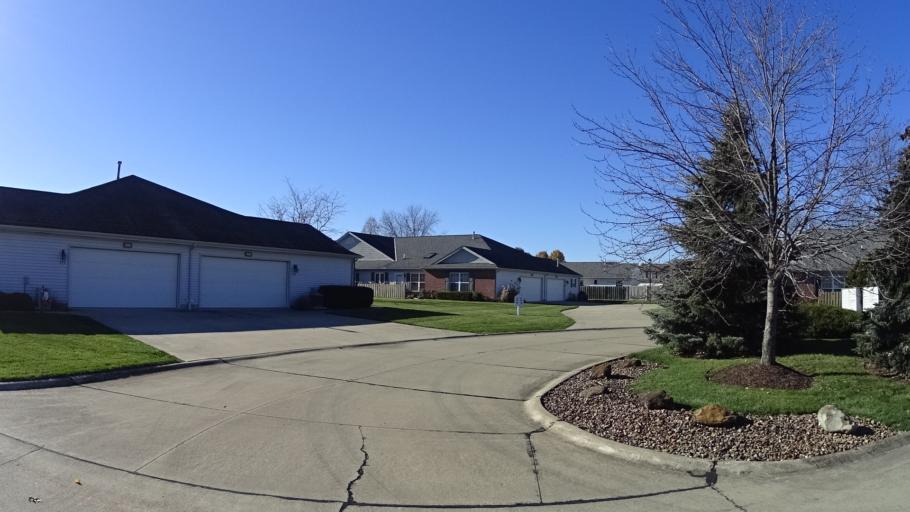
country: US
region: Ohio
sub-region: Lorain County
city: Elyria
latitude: 41.3515
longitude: -82.0714
